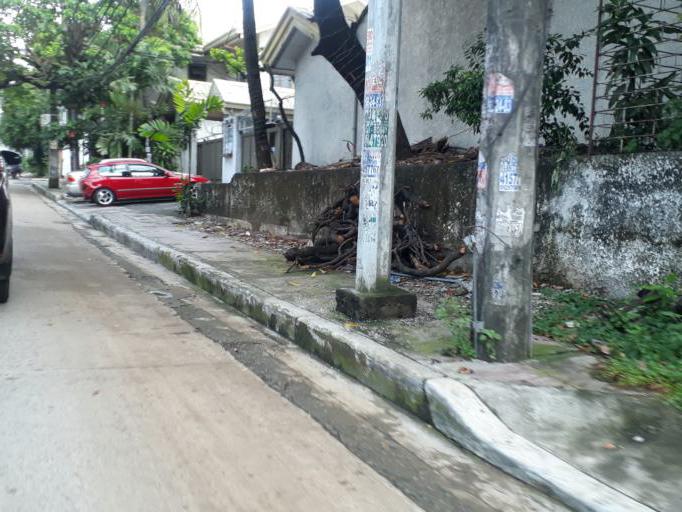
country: PH
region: Metro Manila
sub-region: San Juan
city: San Juan
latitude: 14.6195
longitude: 121.0255
